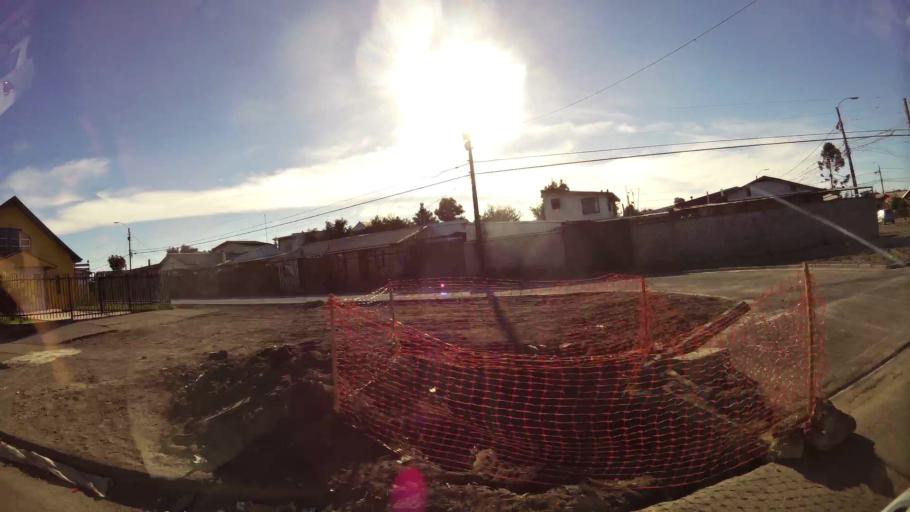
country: CL
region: Biobio
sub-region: Provincia de Concepcion
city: Concepcion
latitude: -36.8290
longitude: -73.1186
